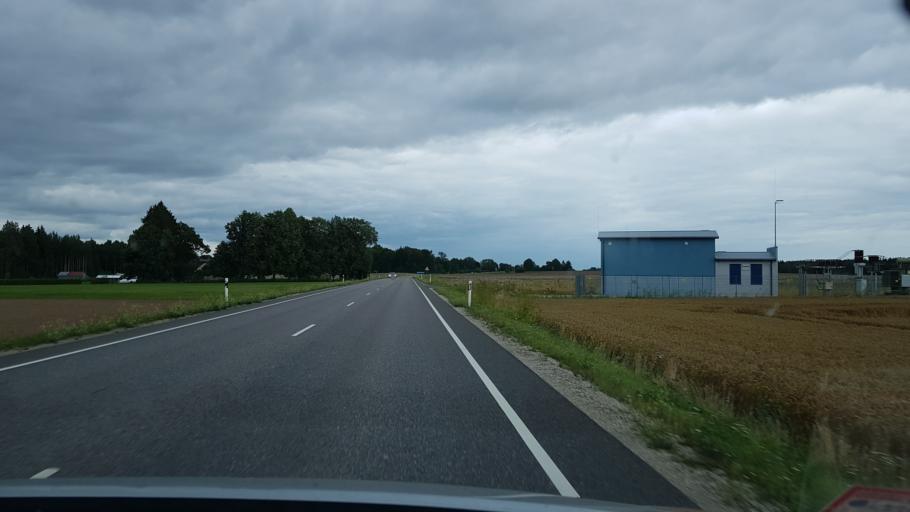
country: EE
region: Tartu
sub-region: Tartu linn
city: Tartu
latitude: 58.4161
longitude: 26.8808
